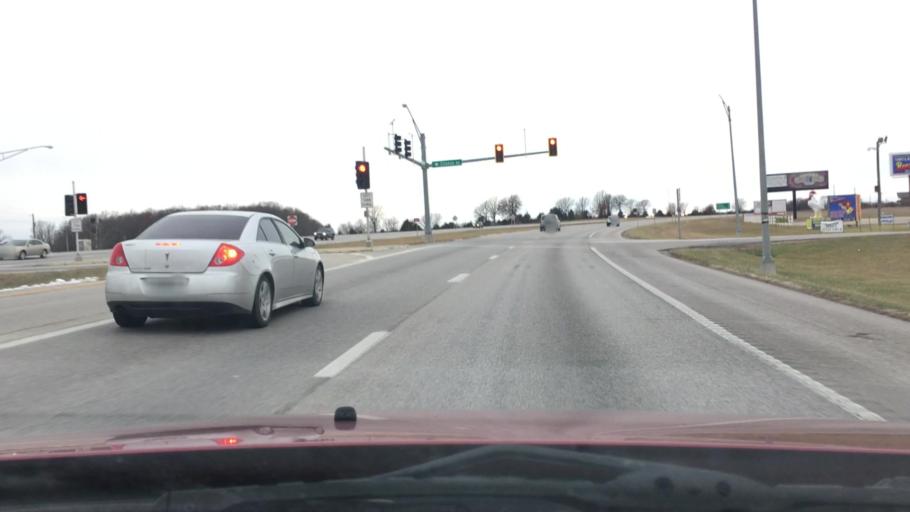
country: US
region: Missouri
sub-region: Webster County
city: Seymour
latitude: 37.1569
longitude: -92.7859
